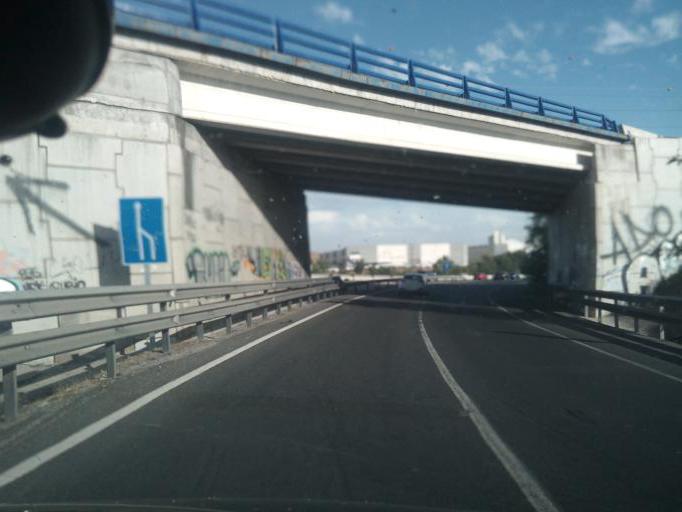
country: ES
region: Madrid
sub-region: Provincia de Madrid
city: Pinto
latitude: 40.2735
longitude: -3.6921
